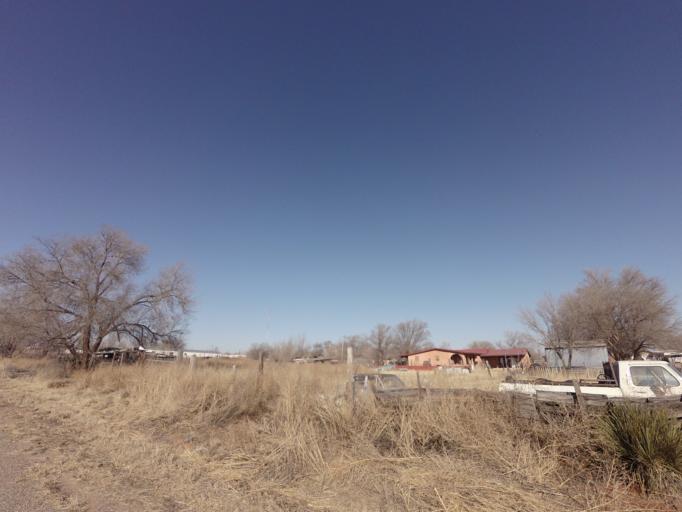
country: US
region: New Mexico
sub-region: Curry County
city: Clovis
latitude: 34.3855
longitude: -103.1820
